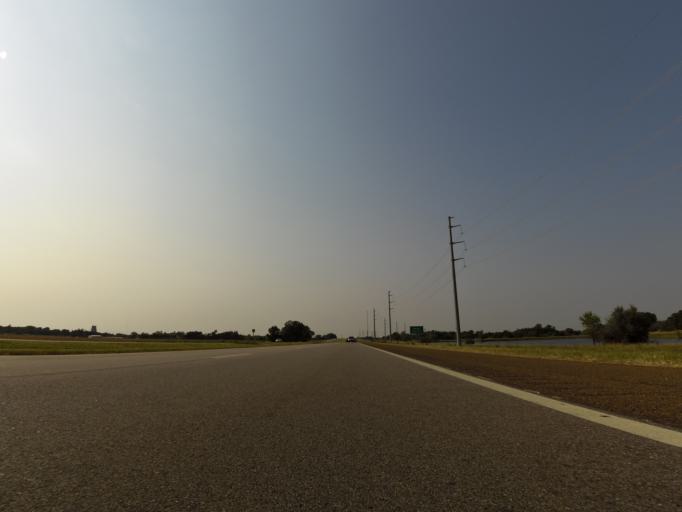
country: US
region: Kansas
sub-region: Sedgwick County
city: Maize
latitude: 37.7748
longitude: -97.4558
